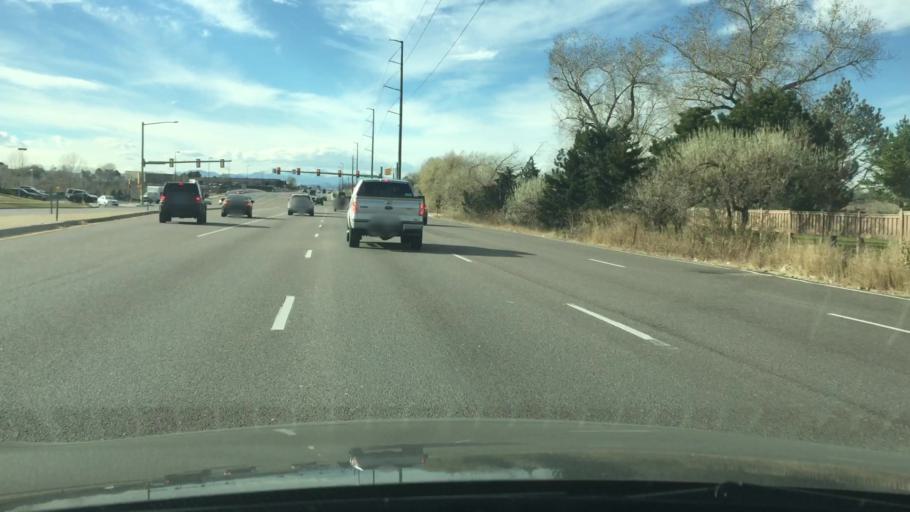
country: US
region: Colorado
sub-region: Arapahoe County
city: Dove Valley
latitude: 39.5951
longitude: -104.8087
